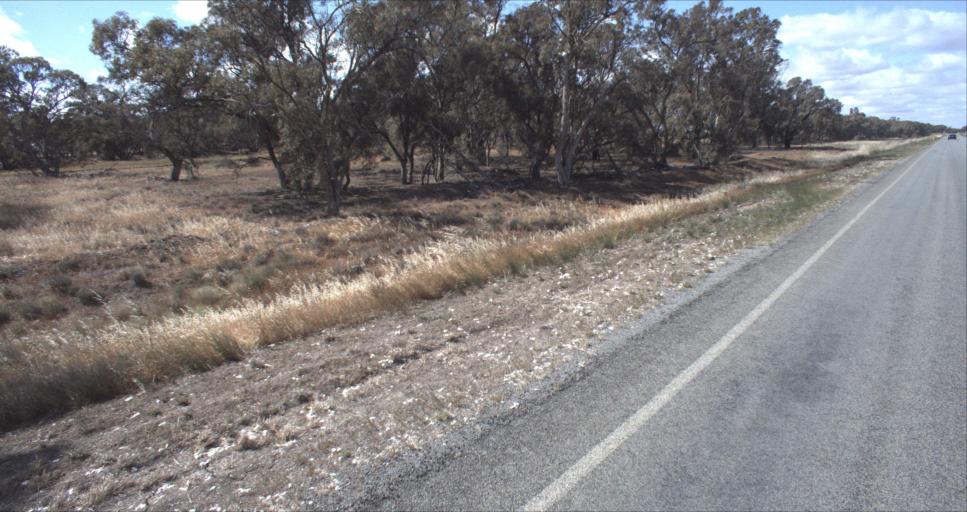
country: AU
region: New South Wales
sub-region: Murrumbidgee Shire
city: Darlington Point
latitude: -34.5458
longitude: 146.1714
